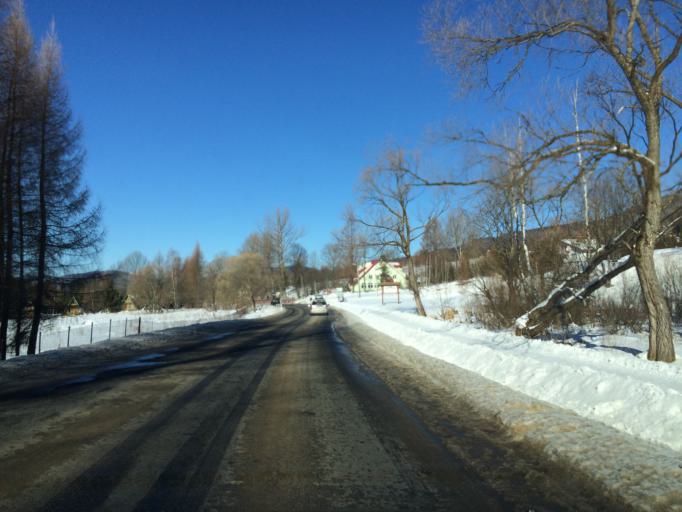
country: PL
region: Subcarpathian Voivodeship
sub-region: Powiat leski
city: Cisna
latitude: 49.1559
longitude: 22.4677
